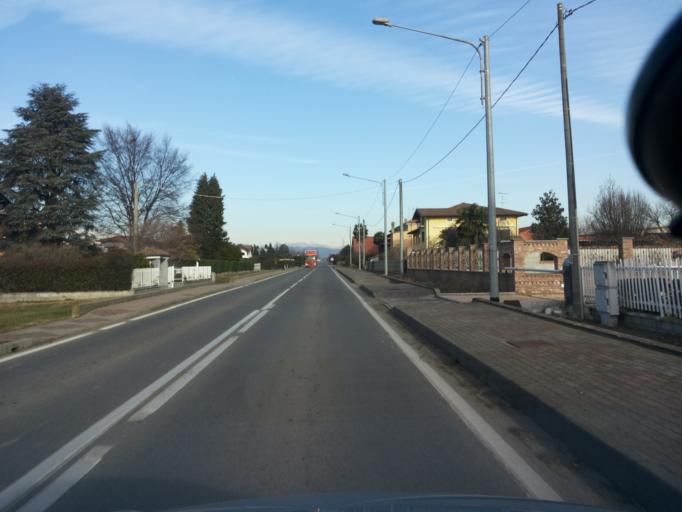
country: IT
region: Piedmont
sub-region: Provincia di Vercelli
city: Ghislarengo
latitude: 45.5353
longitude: 8.3856
